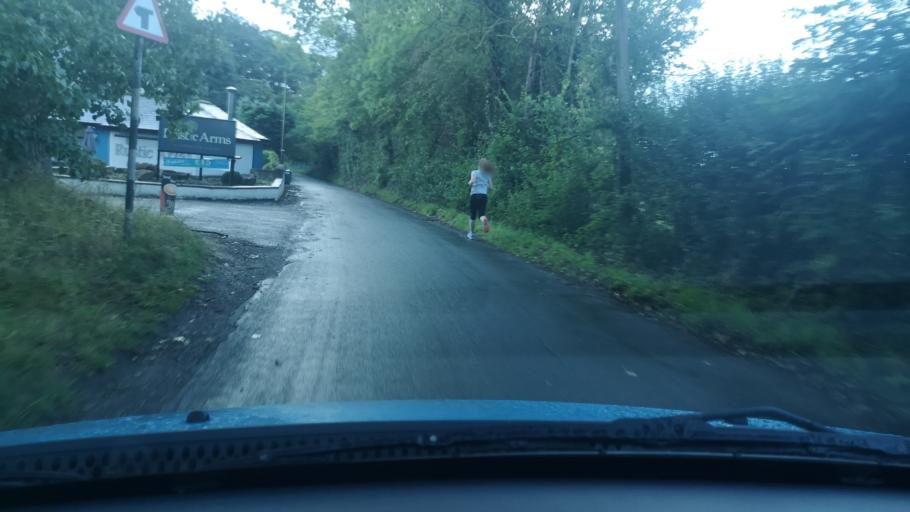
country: GB
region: England
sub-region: City and Borough of Wakefield
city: Low Ackworth
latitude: 53.6578
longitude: -1.3156
